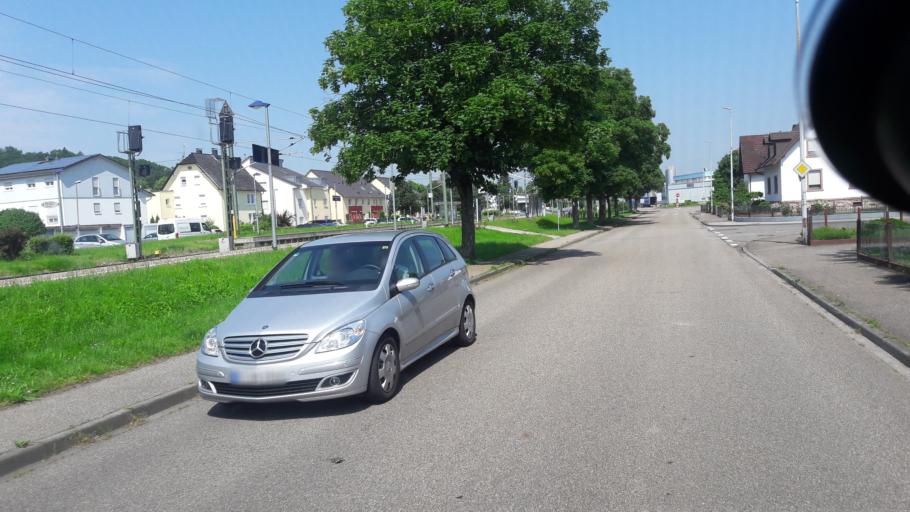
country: DE
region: Baden-Wuerttemberg
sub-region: Karlsruhe Region
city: Bischweier
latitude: 48.8153
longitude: 8.3042
